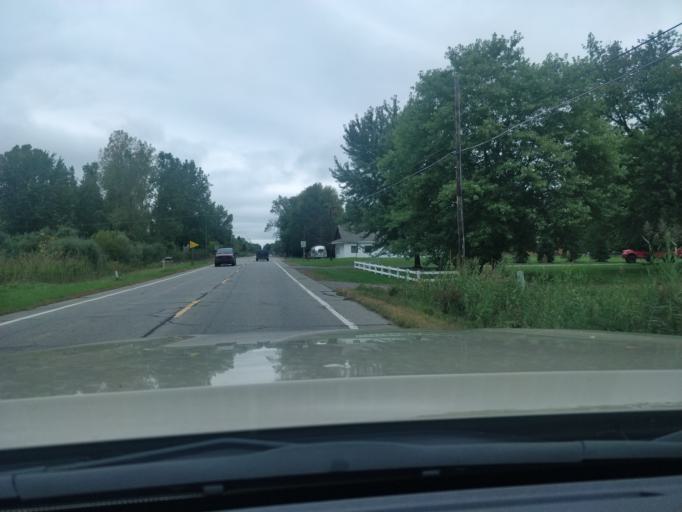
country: US
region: Michigan
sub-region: Wayne County
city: Romulus
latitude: 42.1744
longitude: -83.4032
